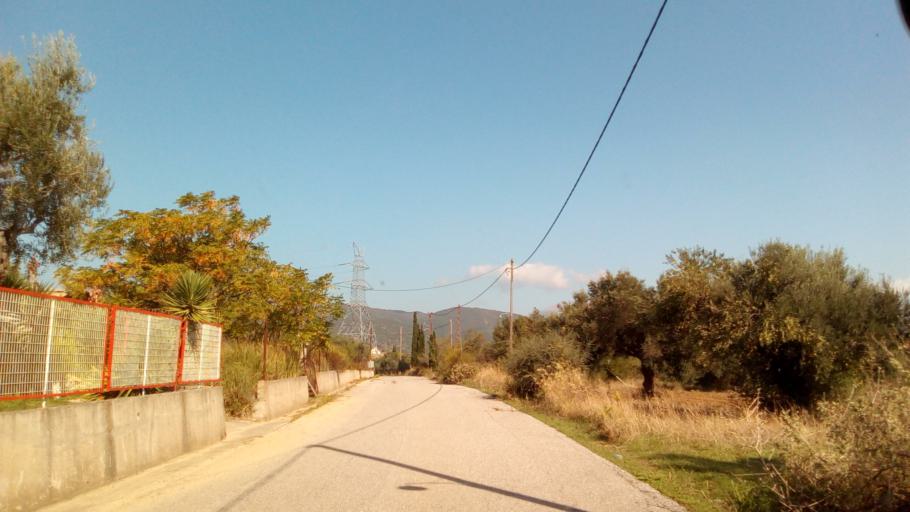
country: GR
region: West Greece
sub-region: Nomos Aitolias kai Akarnanias
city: Antirrio
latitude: 38.3425
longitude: 21.7618
